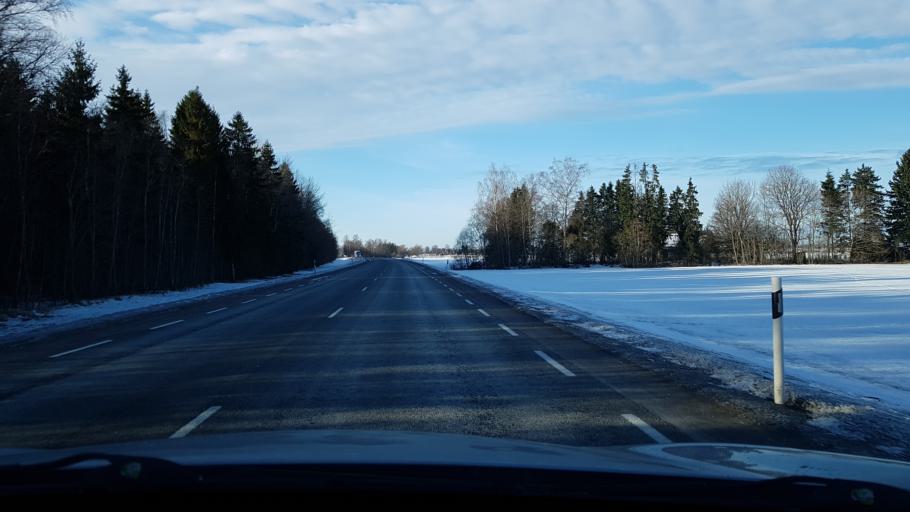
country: EE
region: Viljandimaa
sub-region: Vohma linn
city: Vohma
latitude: 58.6673
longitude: 25.6358
